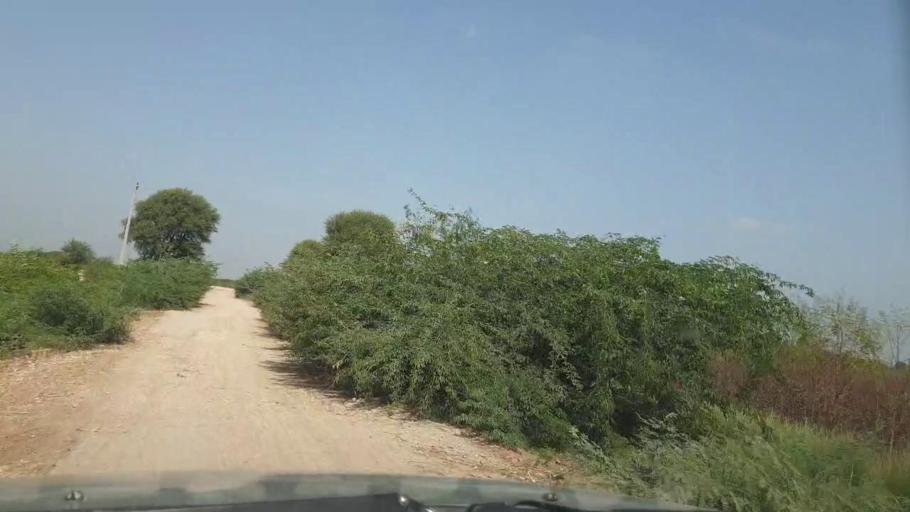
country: PK
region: Sindh
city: Tando Ghulam Ali
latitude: 25.0830
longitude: 68.8020
